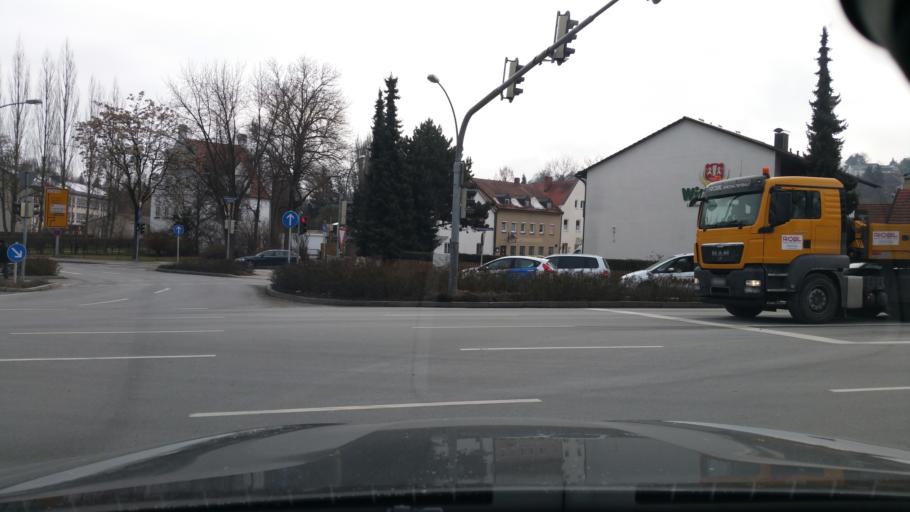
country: DE
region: Bavaria
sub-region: Lower Bavaria
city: Landshut
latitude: 48.5288
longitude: 12.1403
